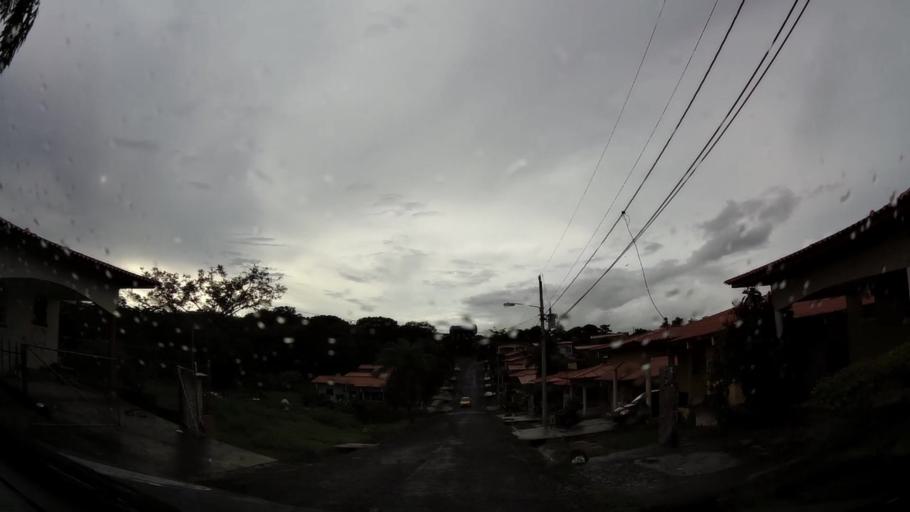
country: PA
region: Veraguas
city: Santiago de Veraguas
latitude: 8.0855
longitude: -80.9874
